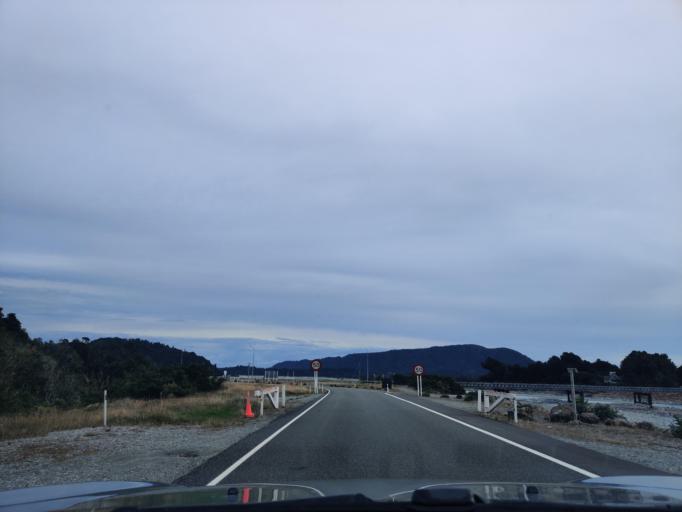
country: NZ
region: West Coast
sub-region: Westland District
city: Hokitika
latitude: -43.3951
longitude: 170.1806
